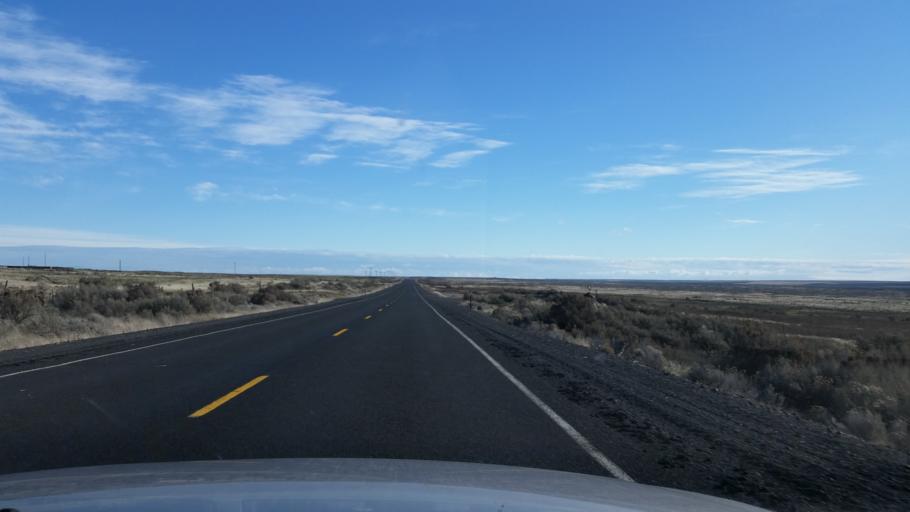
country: US
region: Washington
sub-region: Grant County
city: Warden
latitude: 47.3437
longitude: -118.9166
